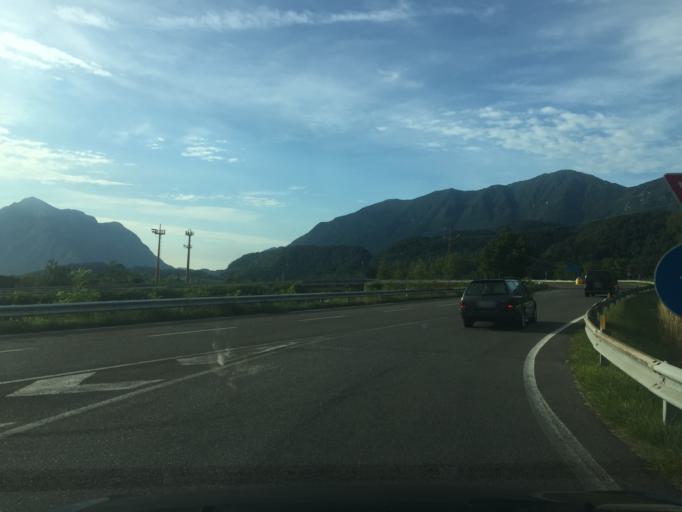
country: IT
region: Friuli Venezia Giulia
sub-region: Provincia di Udine
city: Chiaulis
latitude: 46.4011
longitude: 13.0026
